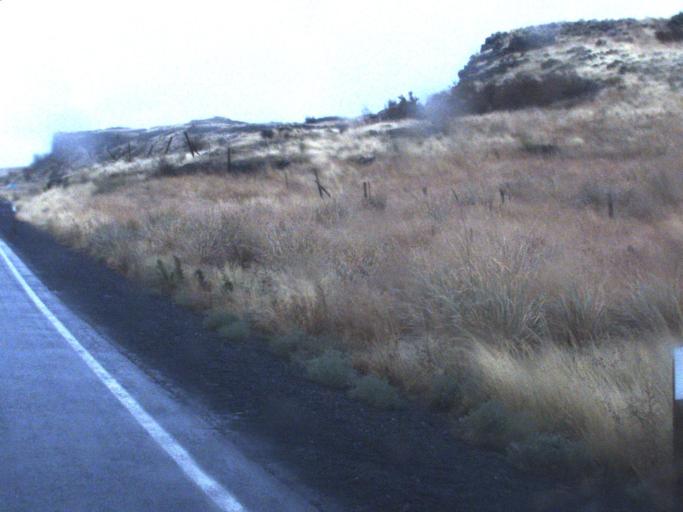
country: US
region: Washington
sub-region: Spokane County
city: Medical Lake
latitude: 47.2582
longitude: -117.9305
